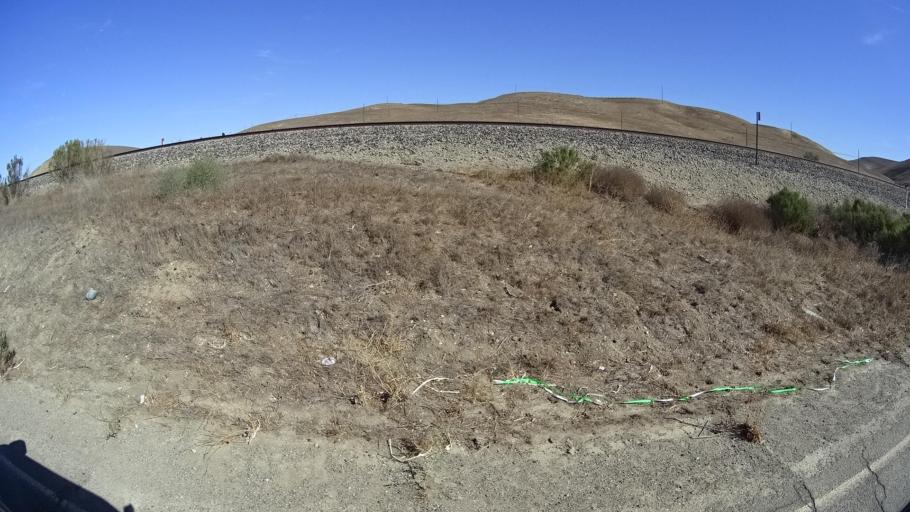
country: US
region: California
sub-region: Monterey County
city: King City
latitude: 36.1043
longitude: -120.9851
